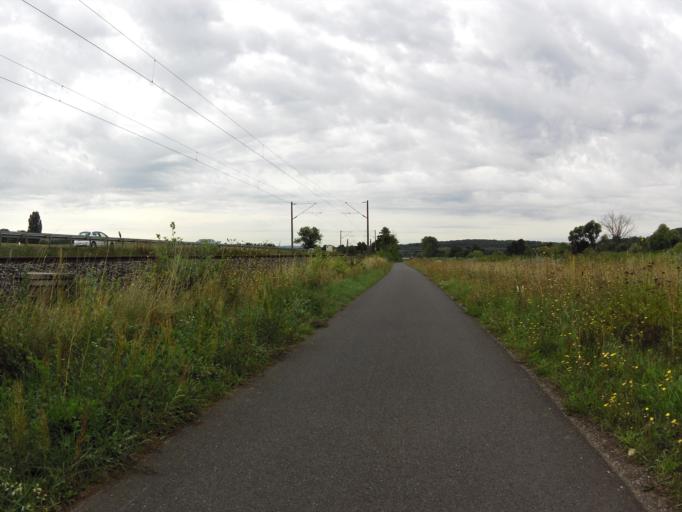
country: DE
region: Bavaria
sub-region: Regierungsbezirk Unterfranken
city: Schonungen
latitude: 50.0324
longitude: 10.3198
